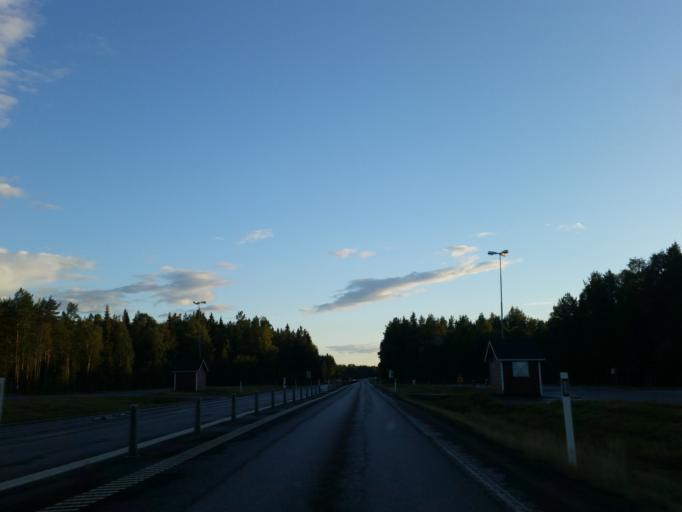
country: SE
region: Vaesterbotten
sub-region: Umea Kommun
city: Saevar
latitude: 63.9126
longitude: 20.5920
